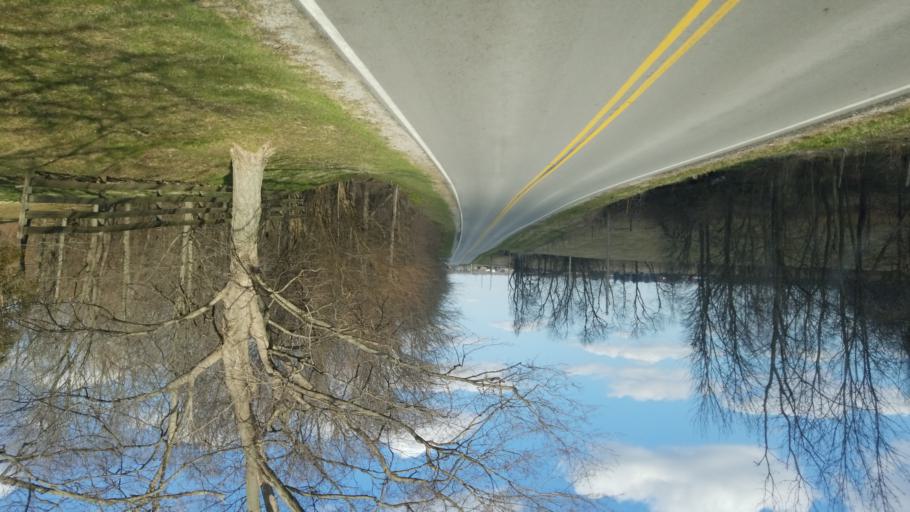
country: US
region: Ohio
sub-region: Highland County
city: Greenfield
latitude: 39.3224
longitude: -83.4187
